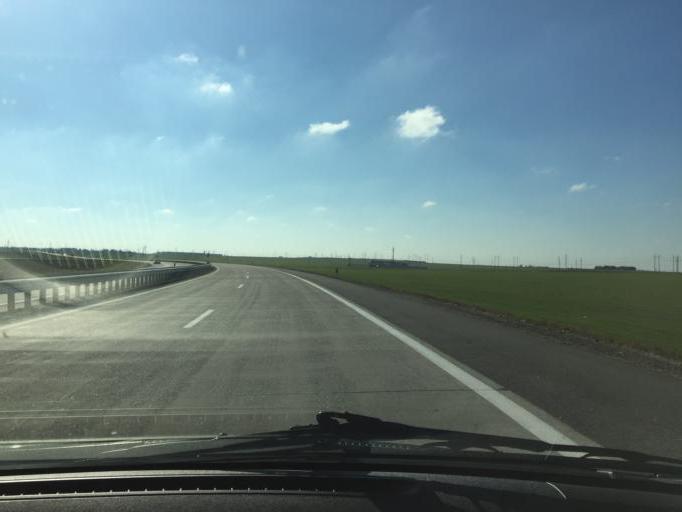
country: BY
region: Minsk
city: Slutsk
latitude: 53.0430
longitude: 27.4913
